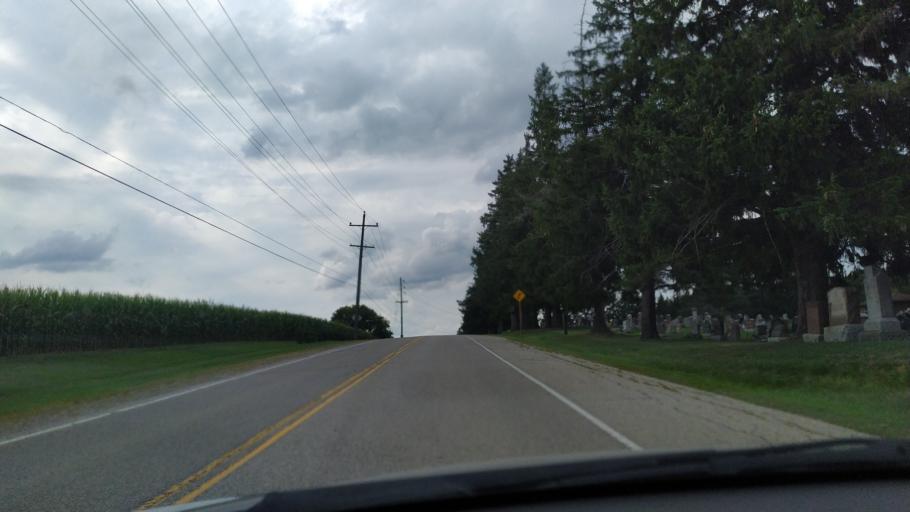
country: CA
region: Ontario
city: Kitchener
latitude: 43.3532
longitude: -80.5408
